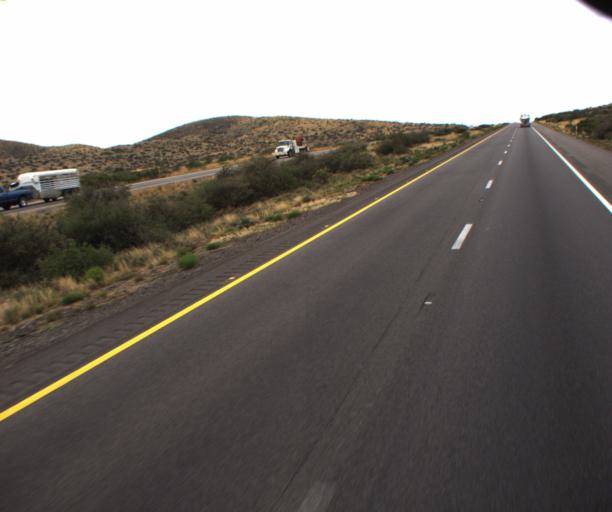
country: US
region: Arizona
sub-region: Cochise County
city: Willcox
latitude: 32.1185
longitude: -110.0183
